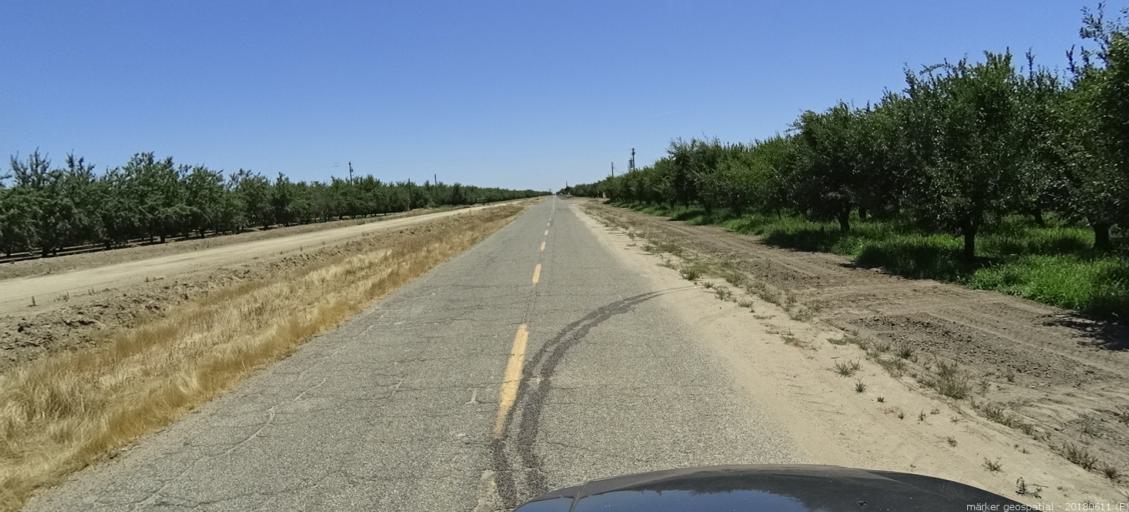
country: US
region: California
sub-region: Madera County
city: Fairmead
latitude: 37.0557
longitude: -120.2115
